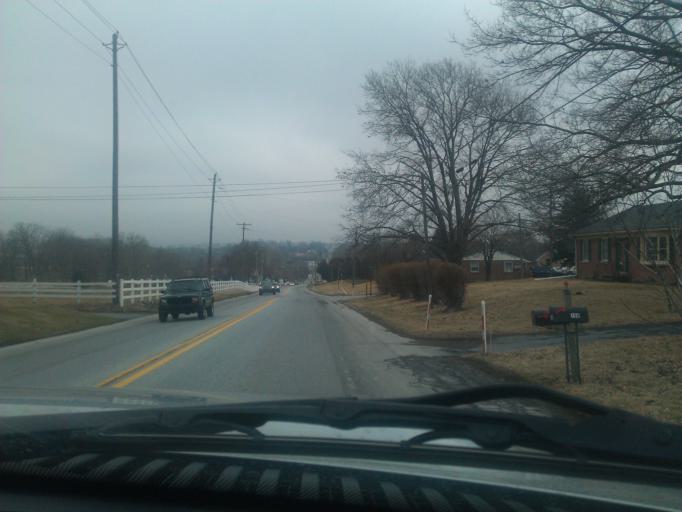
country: US
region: Pennsylvania
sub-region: Lancaster County
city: Strasburg
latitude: 40.0111
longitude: -76.1884
